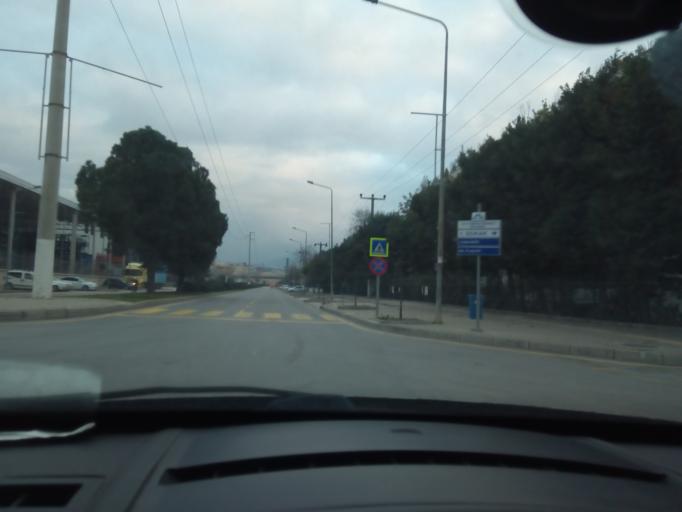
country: TR
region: Bursa
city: Niluefer
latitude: 40.2402
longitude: 28.9653
